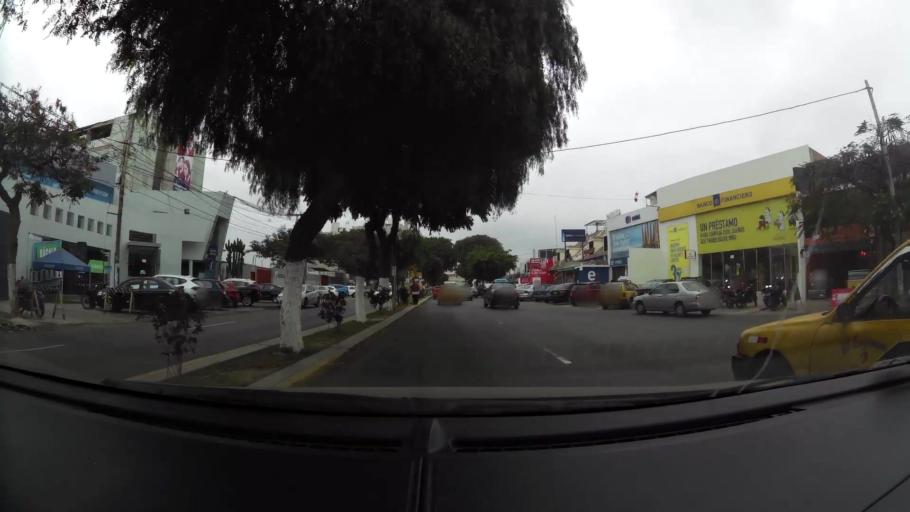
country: PE
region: La Libertad
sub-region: Provincia de Trujillo
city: Trujillo
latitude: -8.1175
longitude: -79.0327
